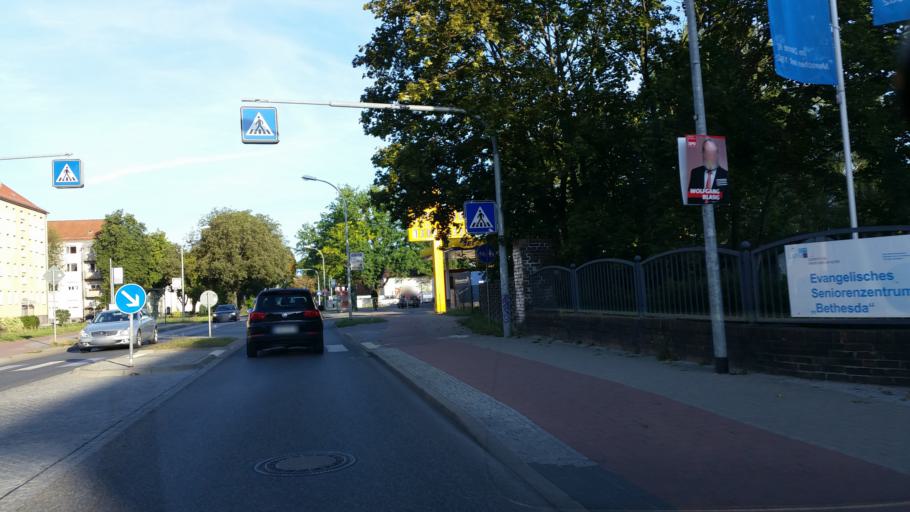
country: DE
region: Brandenburg
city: Teltow
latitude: 52.3953
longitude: 13.2817
